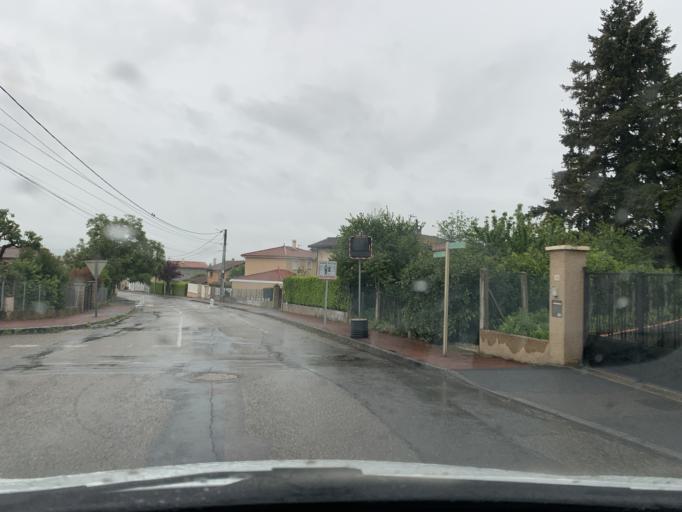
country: FR
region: Rhone-Alpes
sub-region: Departement du Rhone
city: Bully
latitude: 45.8516
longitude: 4.5815
